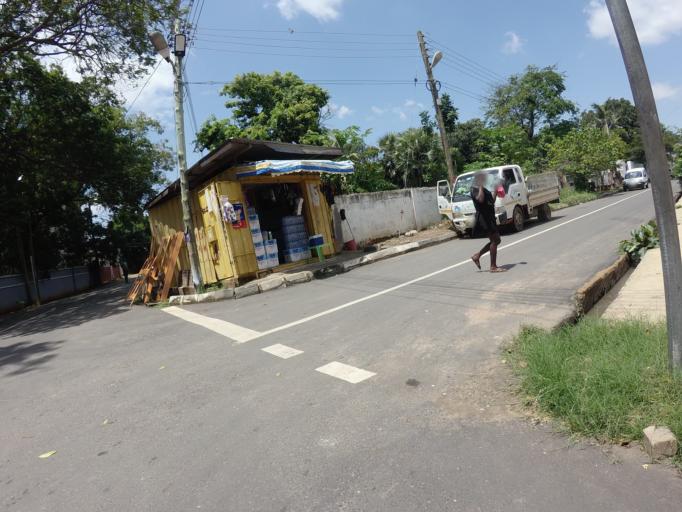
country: GH
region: Greater Accra
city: Accra
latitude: 5.5746
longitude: -0.2014
